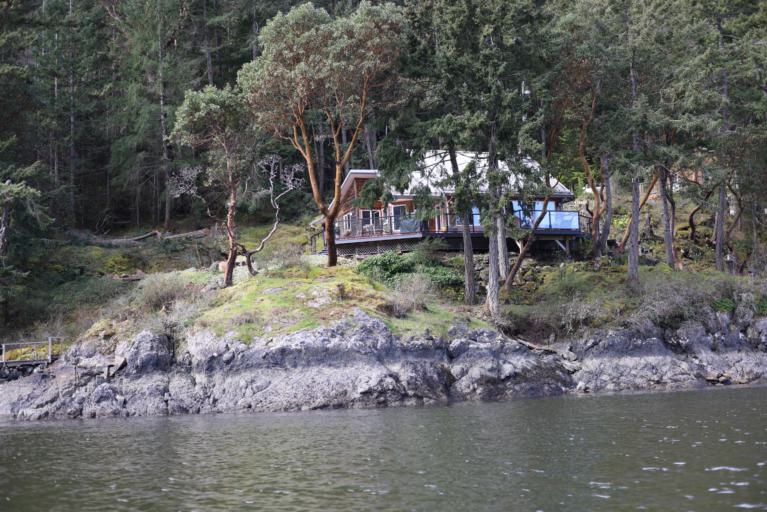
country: CA
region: British Columbia
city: Langford
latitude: 48.5269
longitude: -123.5443
